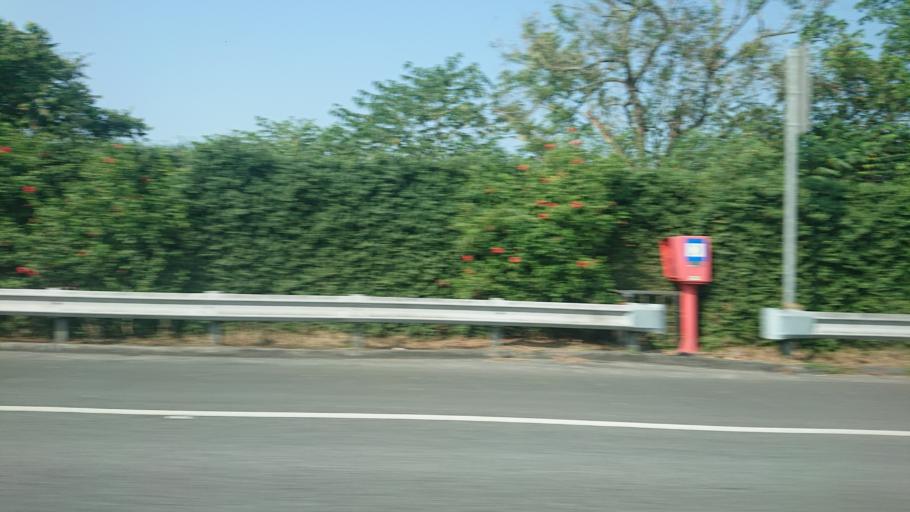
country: TW
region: Taiwan
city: Lugu
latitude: 23.7850
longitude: 120.7041
